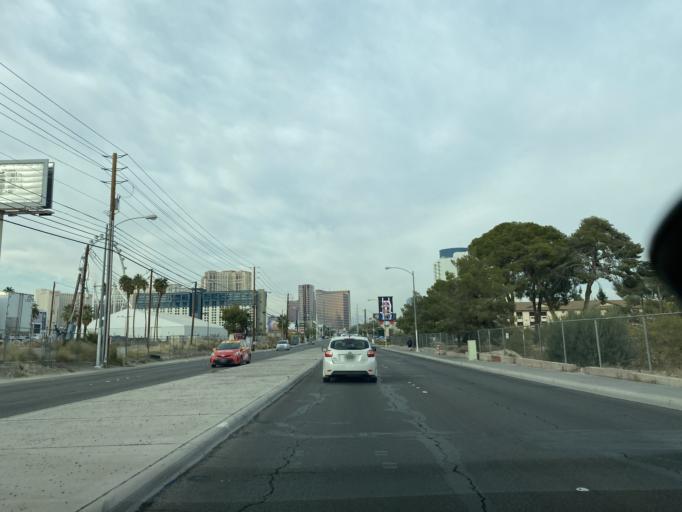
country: US
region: Nevada
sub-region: Clark County
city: Paradise
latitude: 36.1105
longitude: -115.1639
